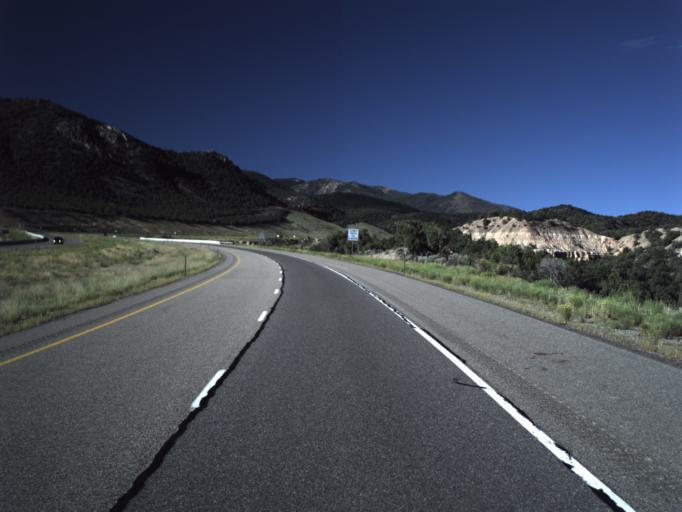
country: US
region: Utah
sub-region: Sevier County
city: Monroe
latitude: 38.5610
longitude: -112.3617
